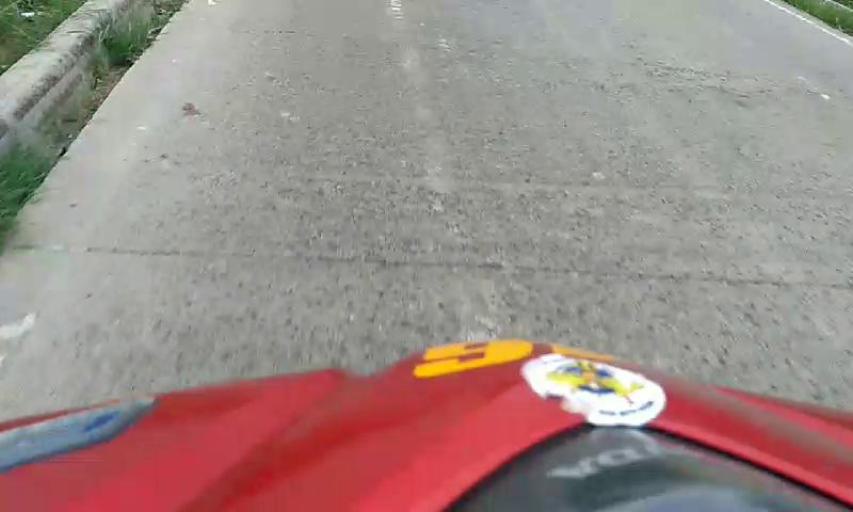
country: ID
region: West Java
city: Bekasi
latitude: -6.1432
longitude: 106.9700
